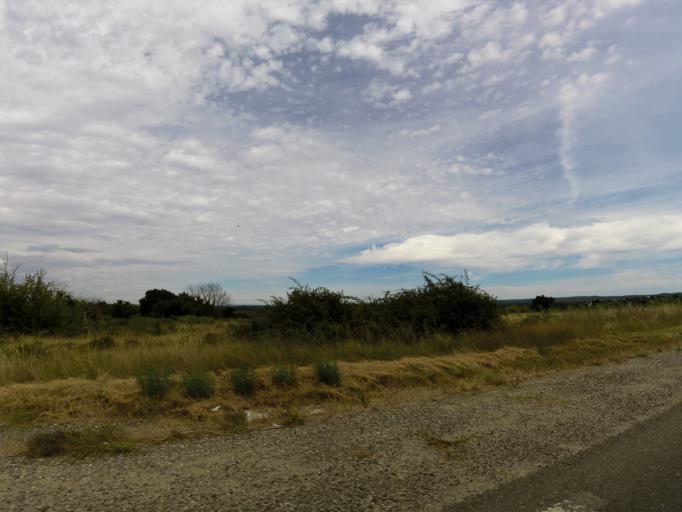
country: FR
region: Languedoc-Roussillon
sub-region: Departement du Gard
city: Saint-Genies-de-Malgoires
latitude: 43.9555
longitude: 4.2134
